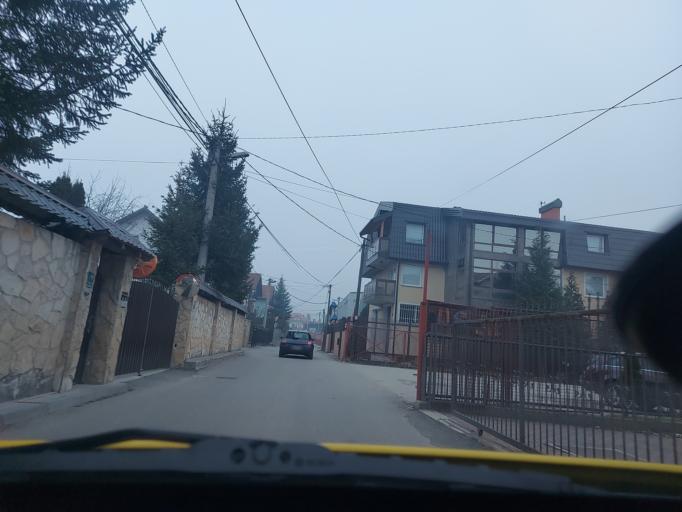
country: BA
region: Federation of Bosnia and Herzegovina
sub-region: Kanton Sarajevo
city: Sarajevo
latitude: 43.8383
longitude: 18.3316
